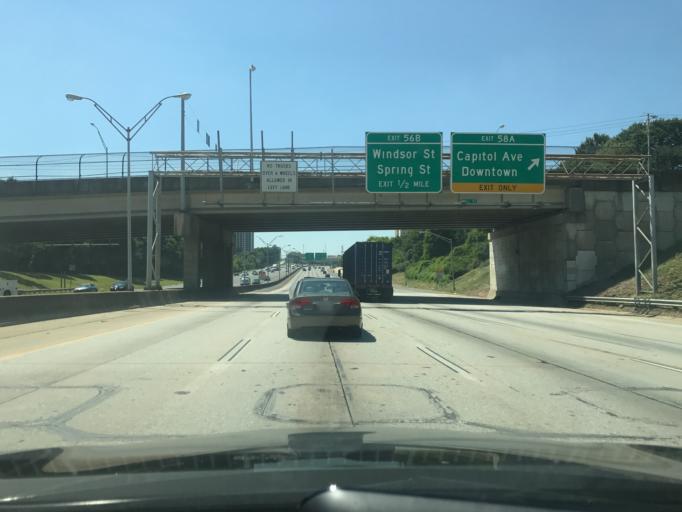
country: US
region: Georgia
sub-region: Fulton County
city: Atlanta
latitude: 33.7435
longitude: -84.3784
